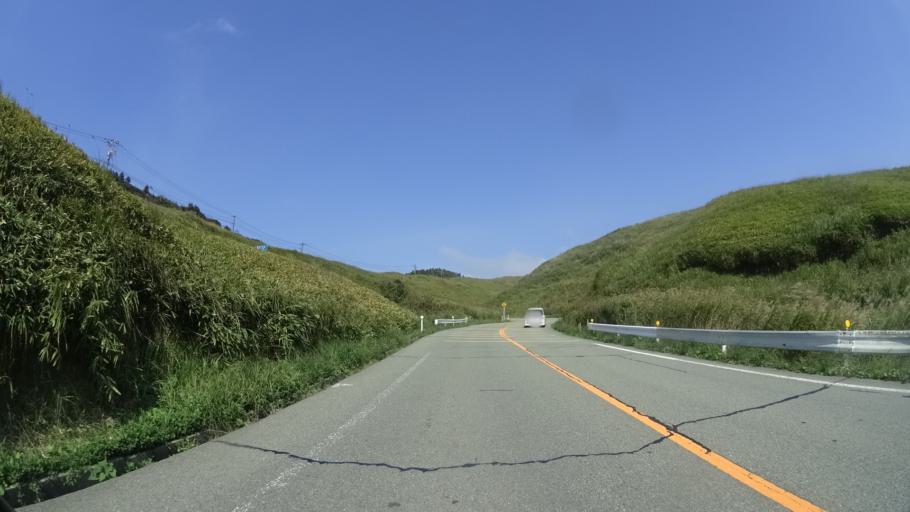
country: JP
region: Kumamoto
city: Ozu
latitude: 32.9142
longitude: 130.9643
